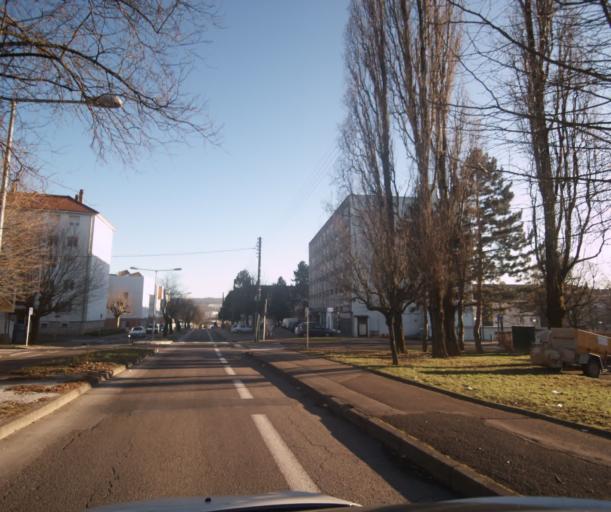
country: FR
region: Franche-Comte
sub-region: Departement du Doubs
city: Besancon
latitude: 47.2623
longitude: 6.0403
